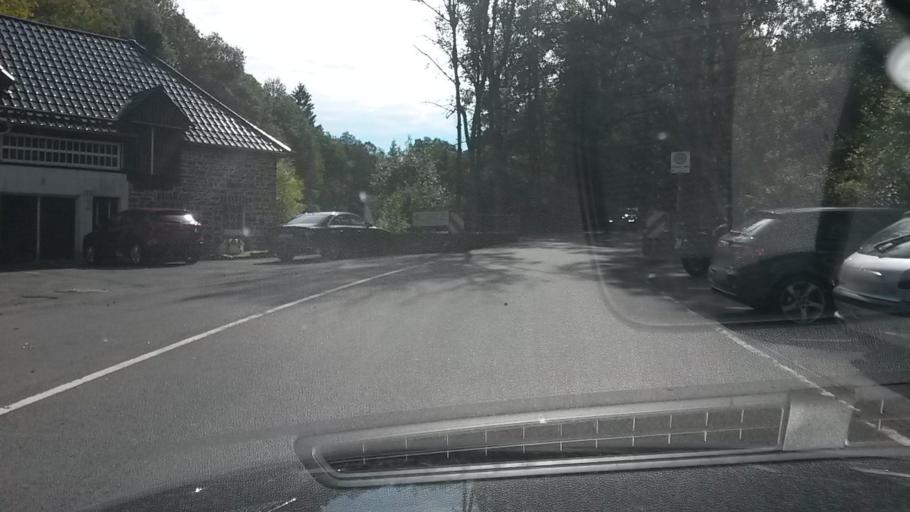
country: DE
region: North Rhine-Westphalia
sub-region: Regierungsbezirk Arnsberg
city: Herscheid
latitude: 51.1903
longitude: 7.7131
